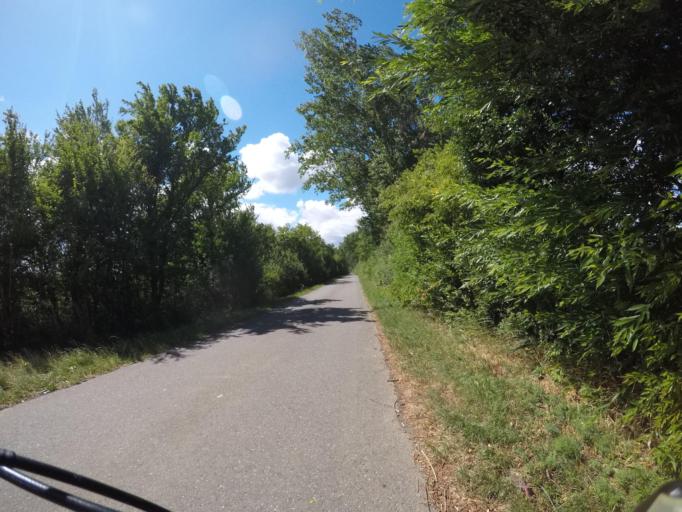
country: DE
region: Lower Saxony
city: Hitzacker
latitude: 53.2052
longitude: 10.9953
